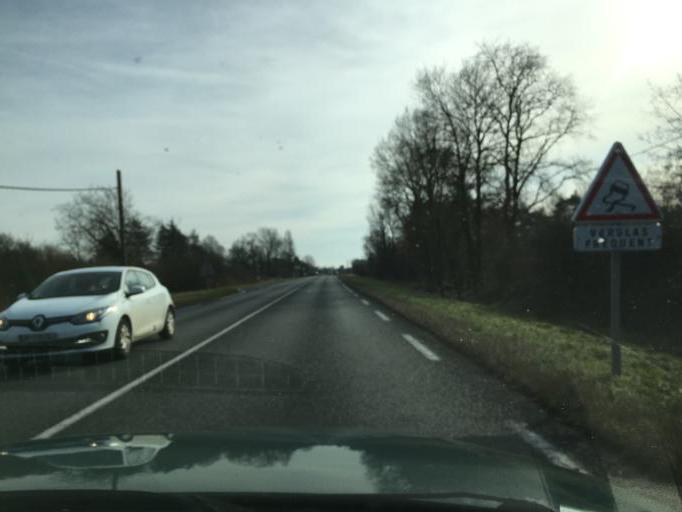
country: FR
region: Centre
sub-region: Departement du Loiret
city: La Ferte-Saint-Aubin
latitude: 47.7743
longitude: 1.9366
